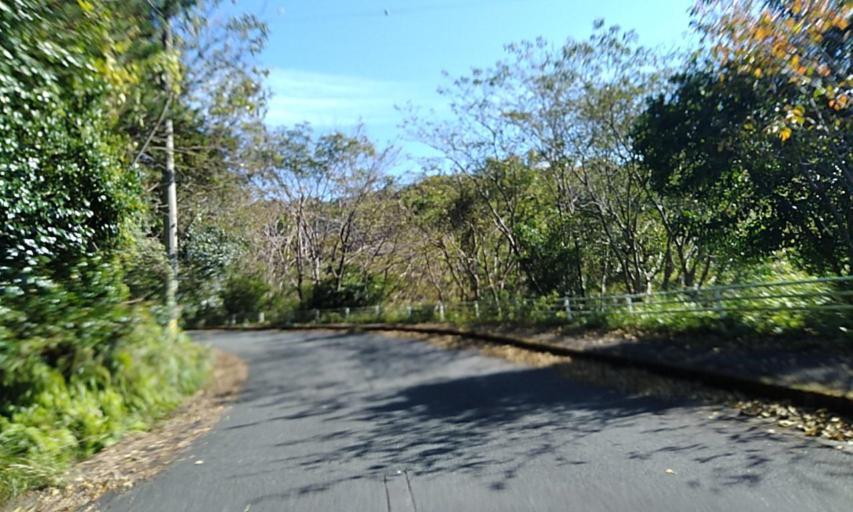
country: JP
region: Mie
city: Owase
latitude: 34.1623
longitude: 136.2853
